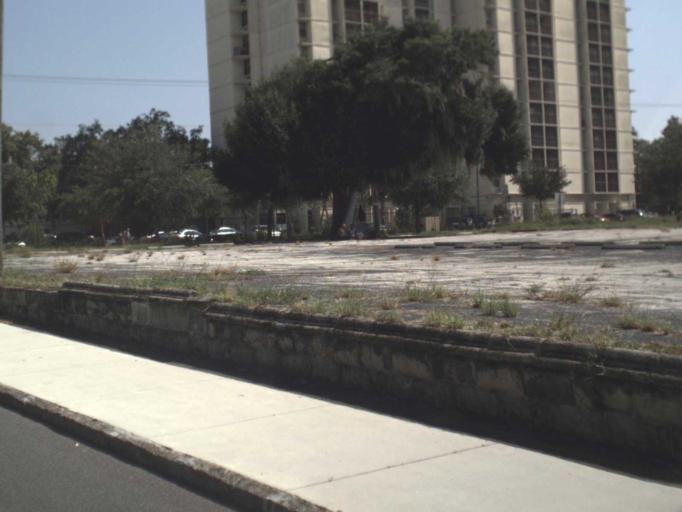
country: US
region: Florida
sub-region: Hillsborough County
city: Tampa
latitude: 27.9609
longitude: -82.4595
